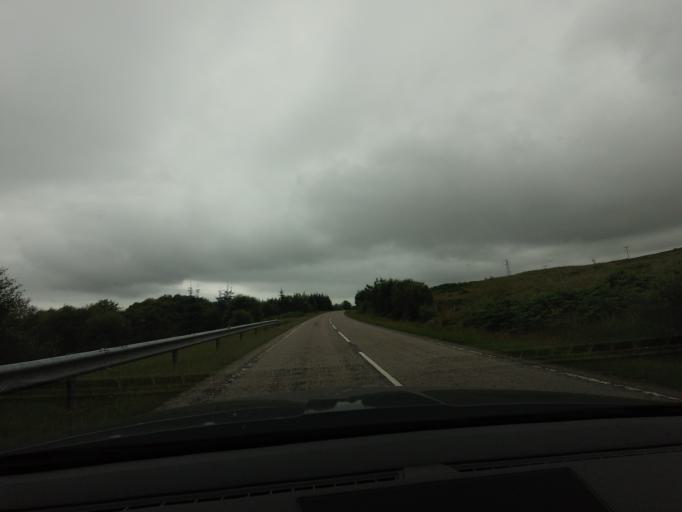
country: GB
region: Scotland
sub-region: Highland
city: Alness
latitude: 57.9874
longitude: -4.4021
